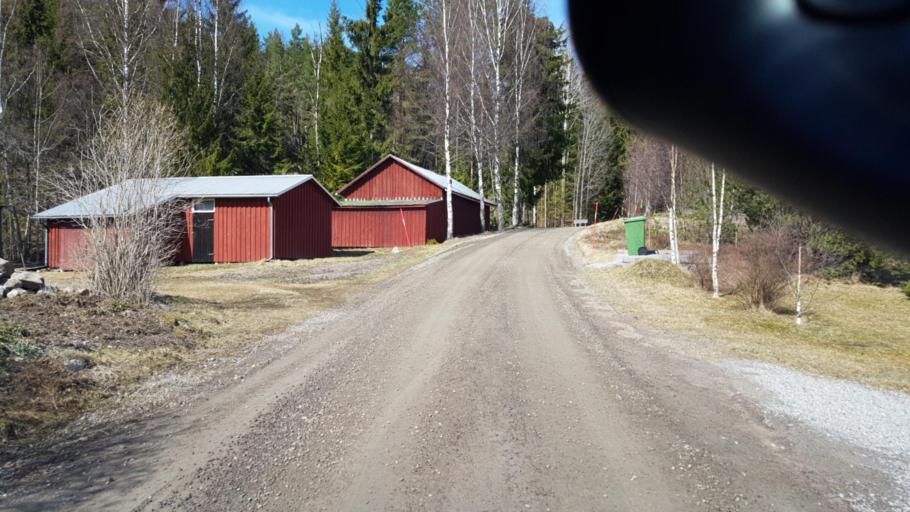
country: SE
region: Vaermland
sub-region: Grums Kommun
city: Grums
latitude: 59.4922
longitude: 12.9267
